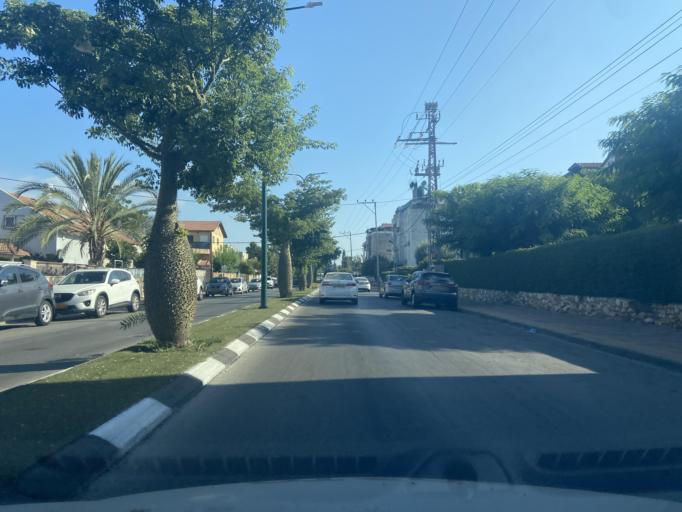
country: IL
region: Central District
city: Yehud
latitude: 32.0321
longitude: 34.8976
